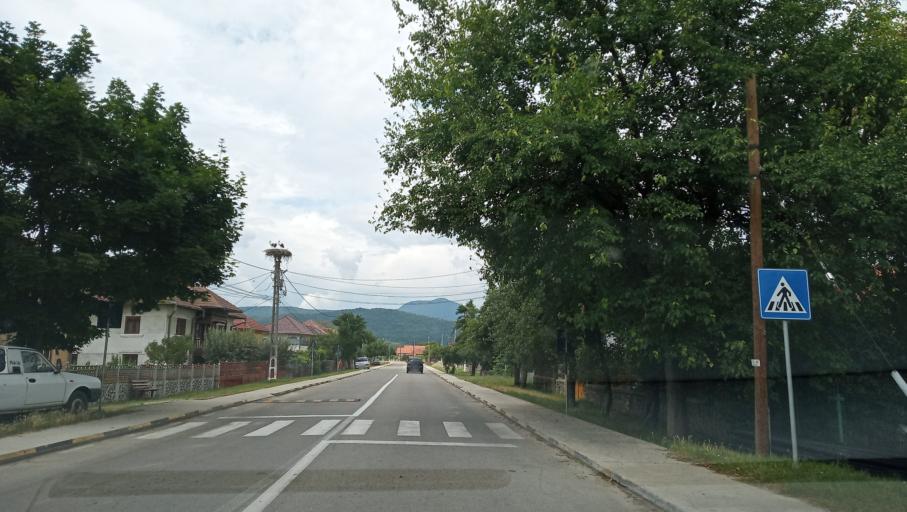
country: RO
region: Gorj
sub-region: Comuna Tismana
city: Tismana
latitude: 45.0433
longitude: 22.9518
